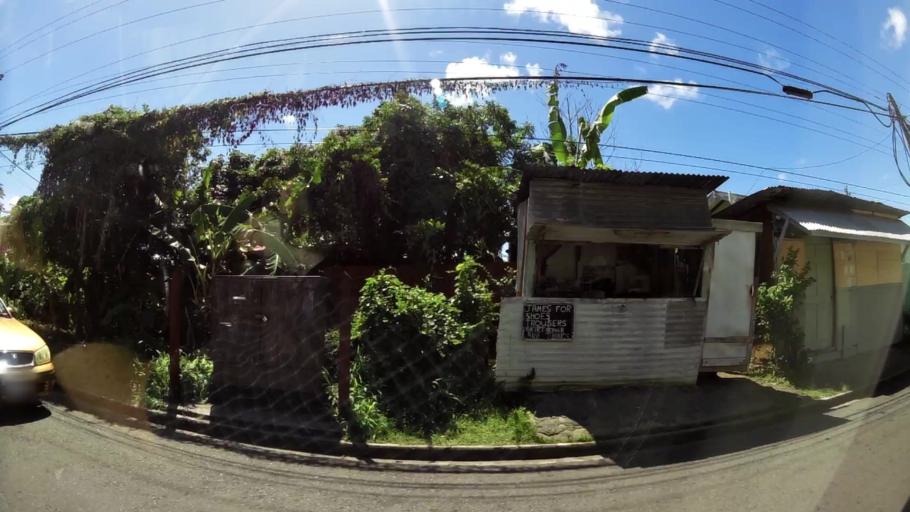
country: TT
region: Tobago
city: Scarborough
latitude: 11.1824
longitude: -60.8016
